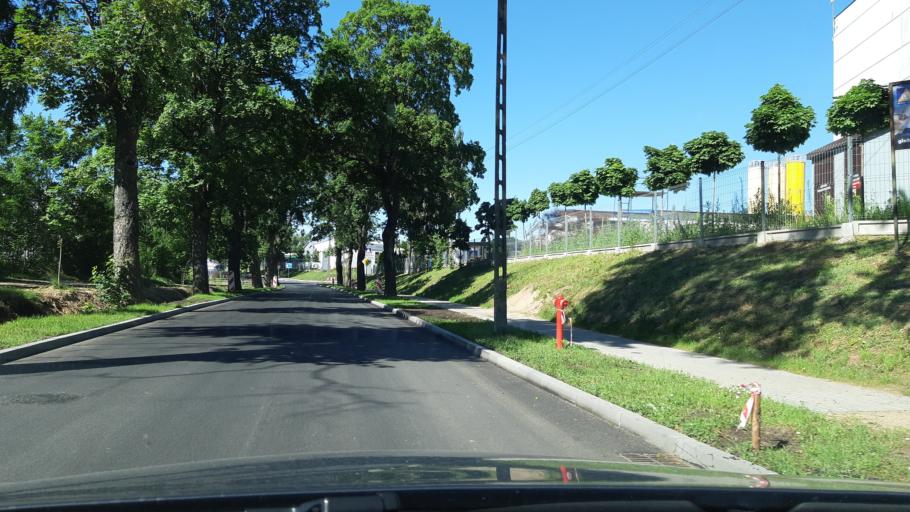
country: PL
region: Warmian-Masurian Voivodeship
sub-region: Powiat mragowski
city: Mragowo
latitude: 53.8541
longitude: 21.2937
